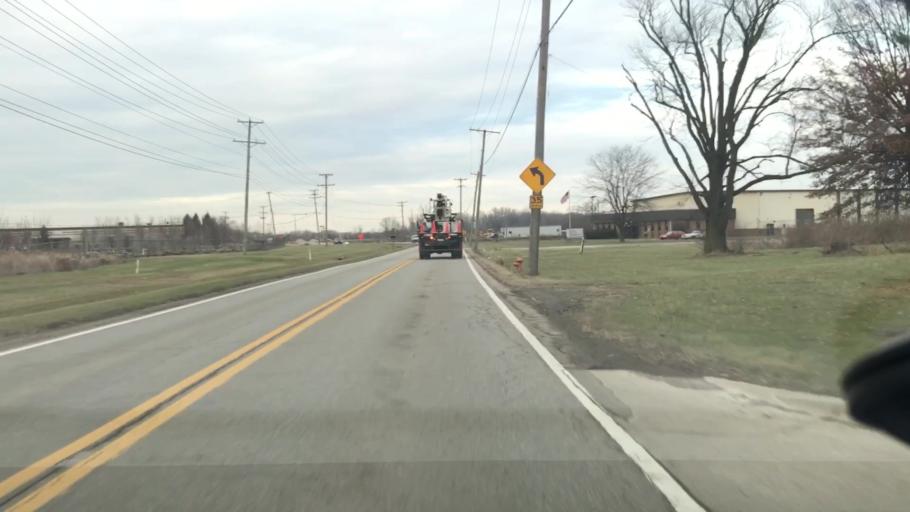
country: US
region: Ohio
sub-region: Franklin County
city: Lincoln Village
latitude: 39.9868
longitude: -83.1370
